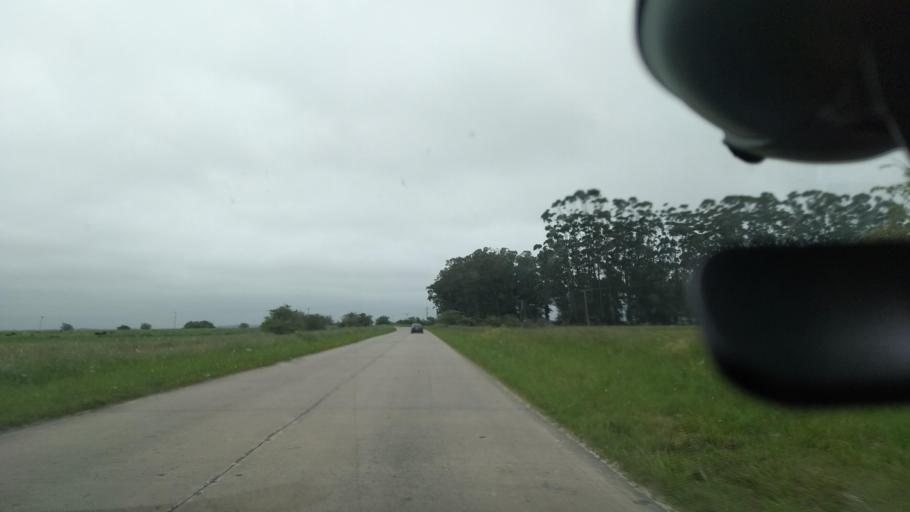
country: AR
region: Buenos Aires
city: Veronica
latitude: -35.5781
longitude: -57.2788
